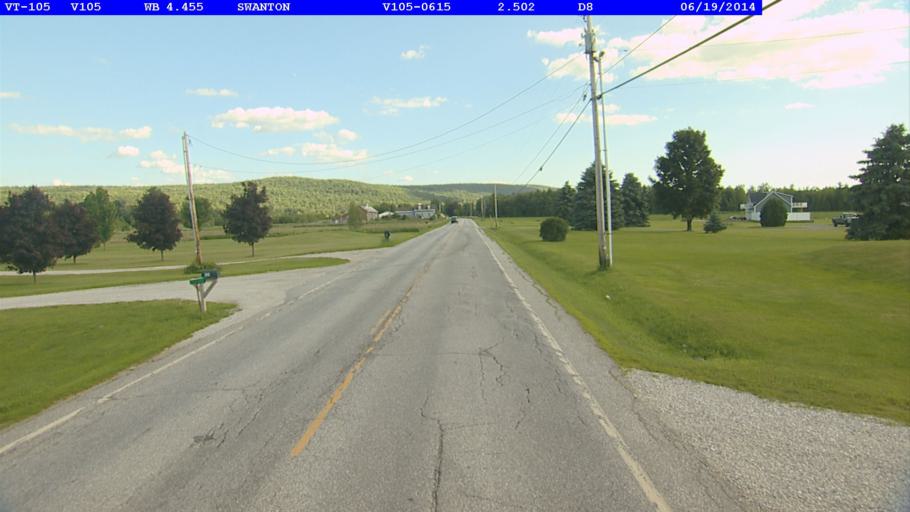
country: US
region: Vermont
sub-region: Franklin County
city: Saint Albans
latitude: 44.8685
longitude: -73.0328
